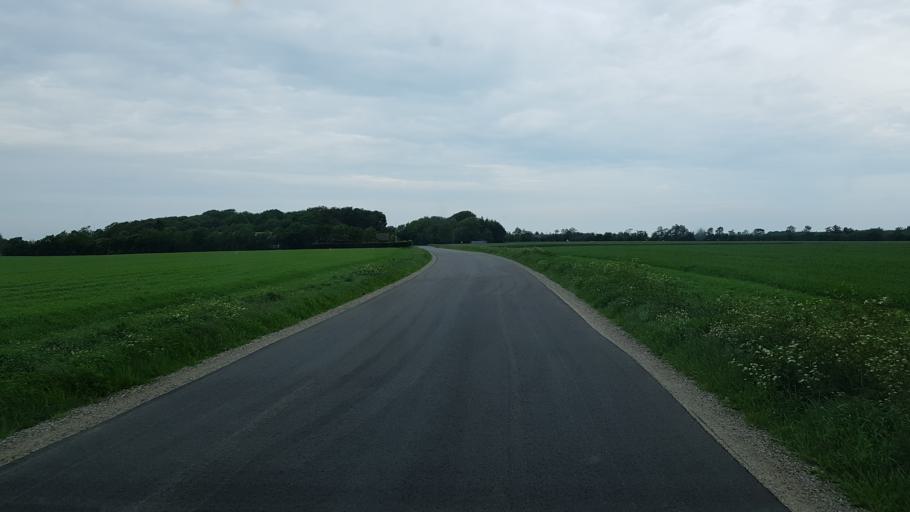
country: DK
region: South Denmark
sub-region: Varde Kommune
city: Oksbol
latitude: 55.7406
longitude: 8.3742
